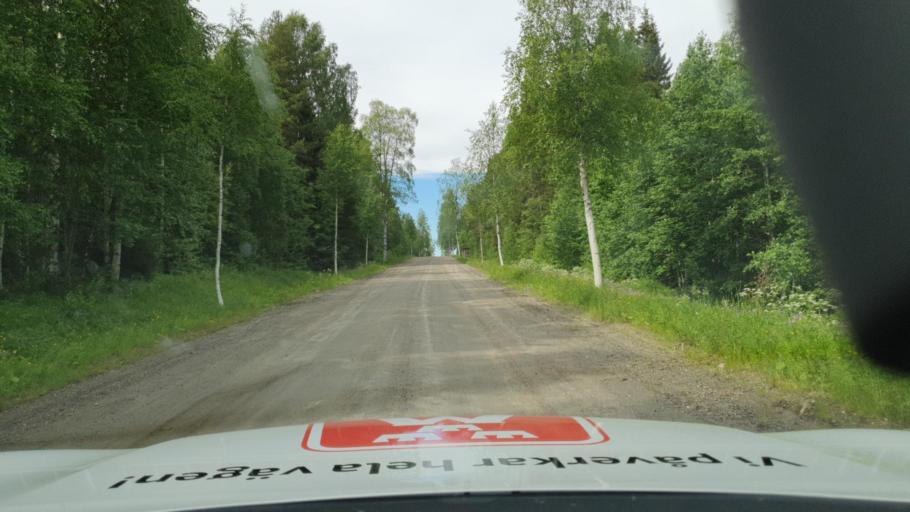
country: SE
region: Vaesterbotten
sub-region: Skelleftea Kommun
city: Burtraesk
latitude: 64.4732
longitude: 20.4489
